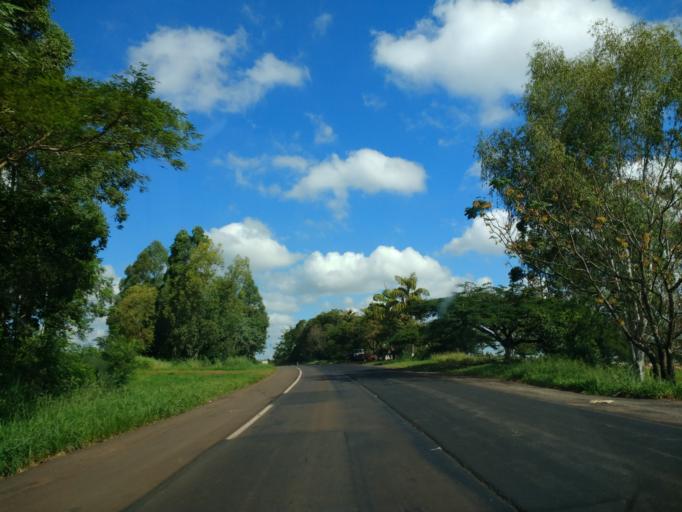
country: BR
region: Parana
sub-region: Umuarama
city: Umuarama
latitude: -23.8707
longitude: -53.3948
